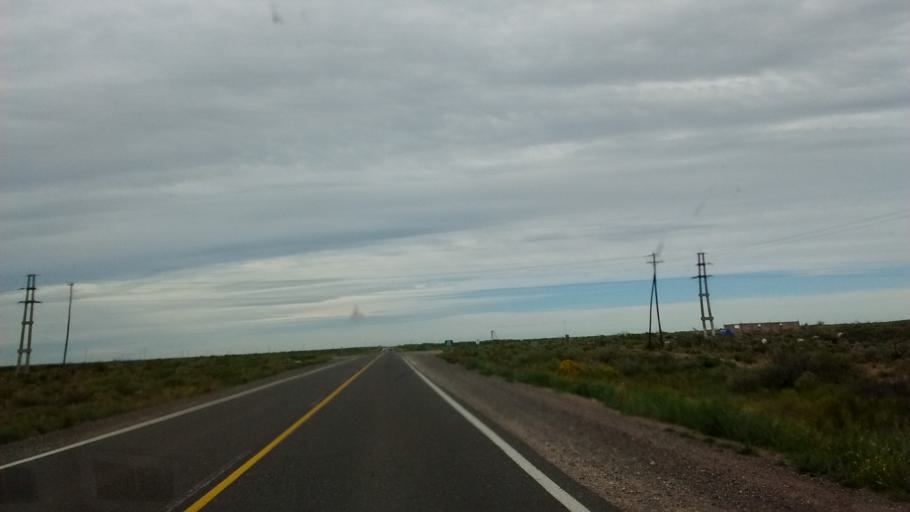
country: AR
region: Rio Negro
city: Catriel
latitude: -38.2124
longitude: -67.9772
